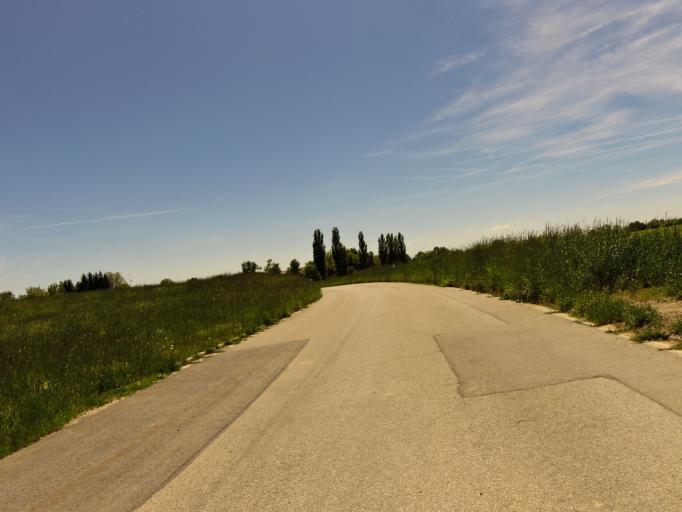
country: DE
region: Bavaria
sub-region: Upper Bavaria
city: Langenbach
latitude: 48.4147
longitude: 11.8320
